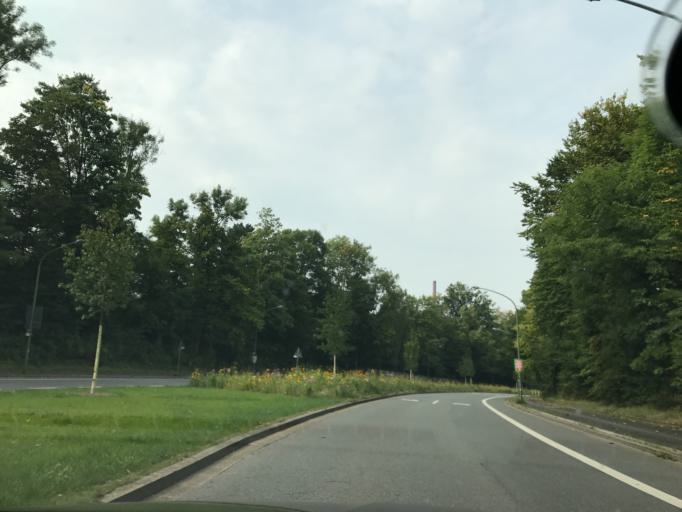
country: DE
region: North Rhine-Westphalia
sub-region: Regierungsbezirk Dusseldorf
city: Essen
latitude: 51.4233
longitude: 7.0173
